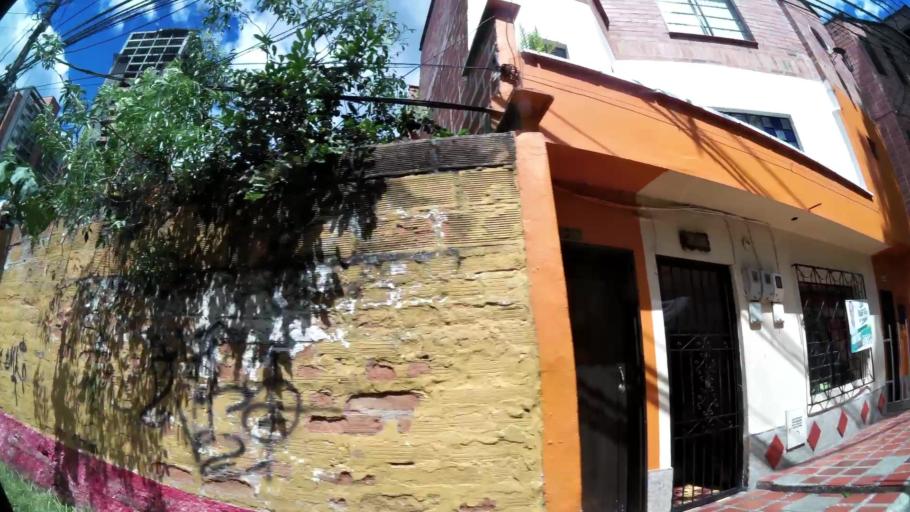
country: CO
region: Antioquia
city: Sabaneta
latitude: 6.1451
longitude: -75.6167
